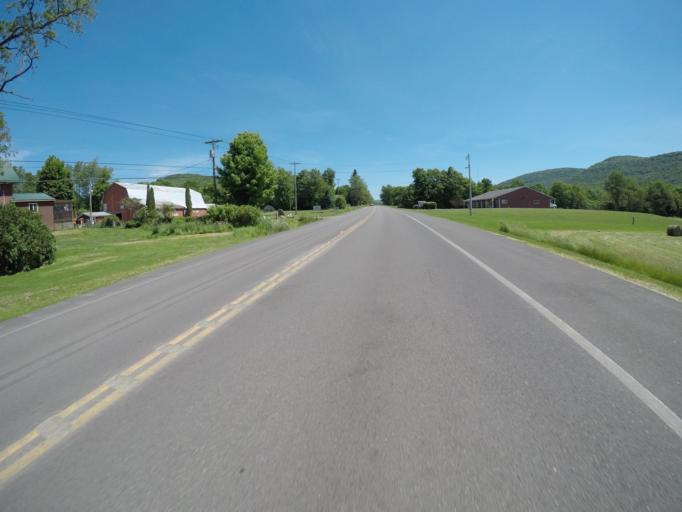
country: US
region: New York
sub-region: Delaware County
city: Walton
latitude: 42.1796
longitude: -75.0165
